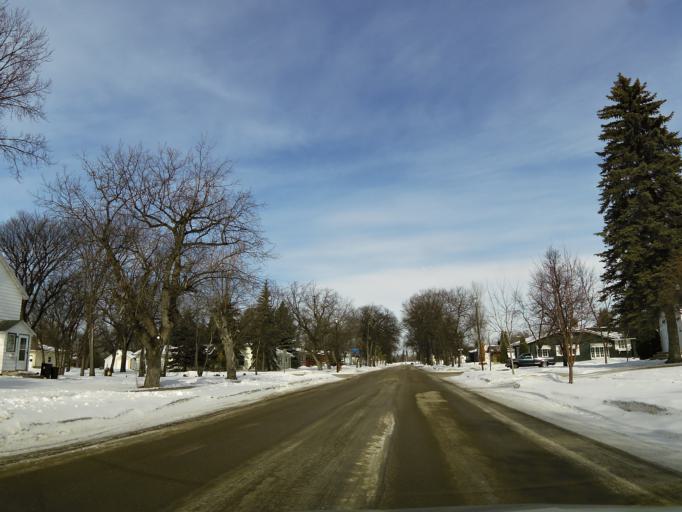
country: US
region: North Dakota
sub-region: Walsh County
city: Grafton
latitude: 48.4160
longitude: -97.4173
